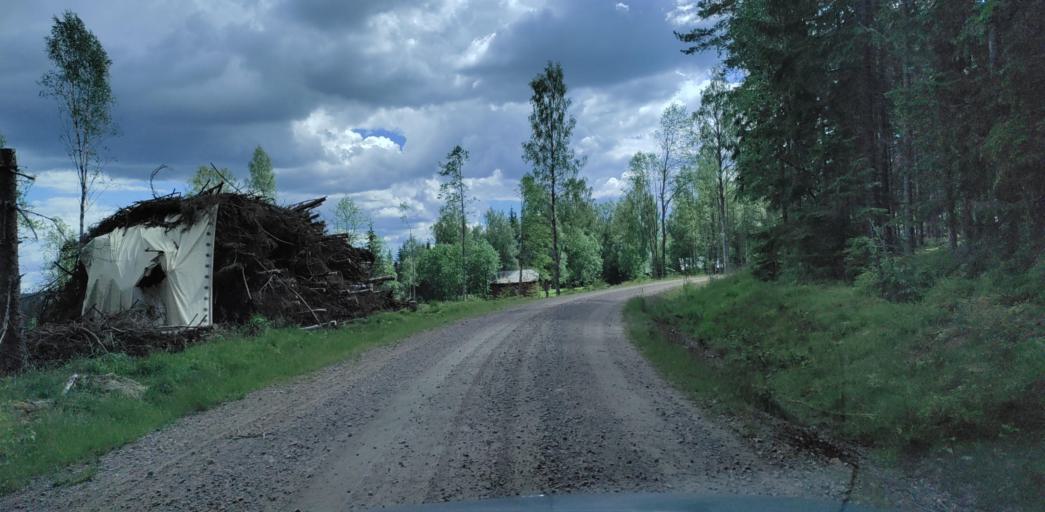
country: SE
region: Vaermland
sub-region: Hagfors Kommun
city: Ekshaerad
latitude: 60.0520
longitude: 13.3105
